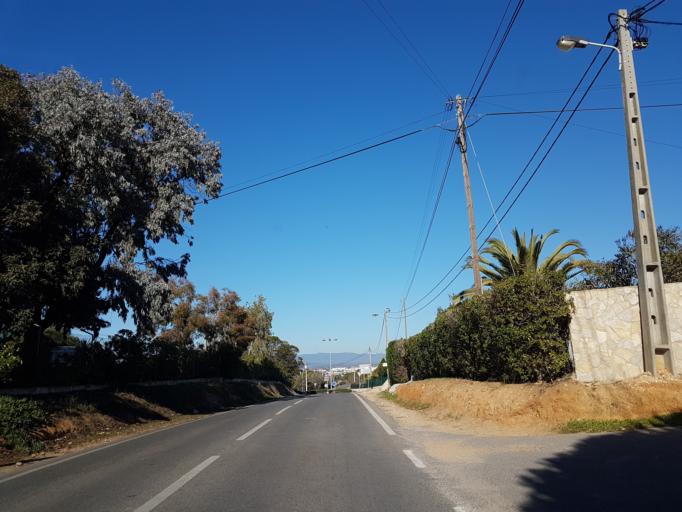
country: PT
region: Faro
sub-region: Lagoa
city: Carvoeiro
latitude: 37.1007
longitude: -8.4435
